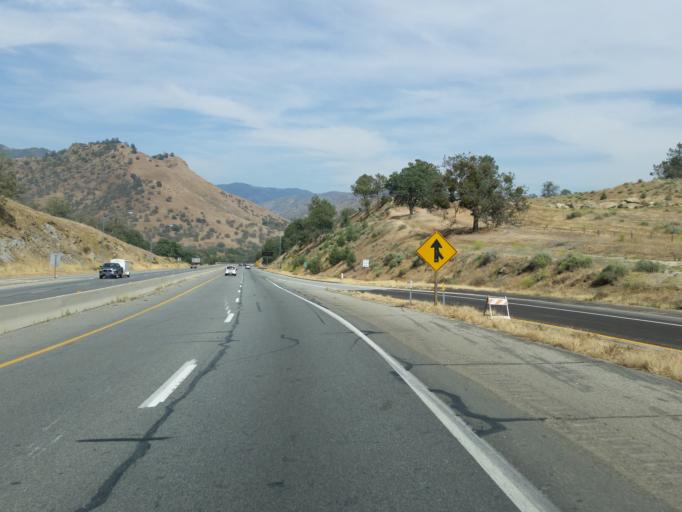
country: US
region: California
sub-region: Kern County
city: Bear Valley Springs
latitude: 35.2407
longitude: -118.5867
